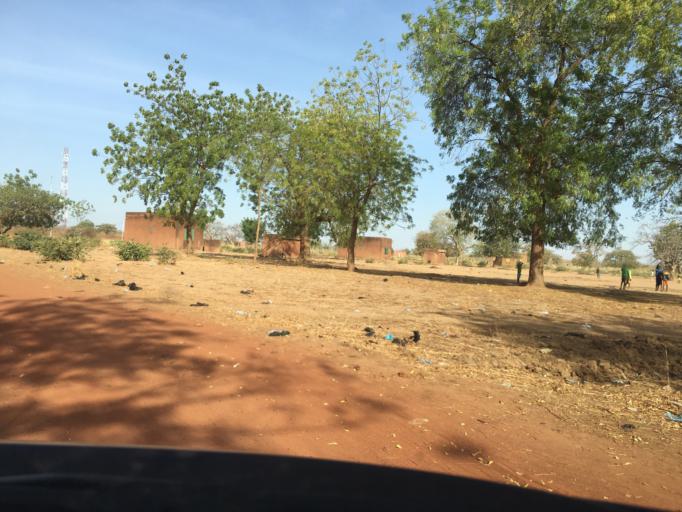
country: BF
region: Plateau-Central
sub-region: Province du Kourweogo
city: Bousse
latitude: 12.5578
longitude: -1.8950
